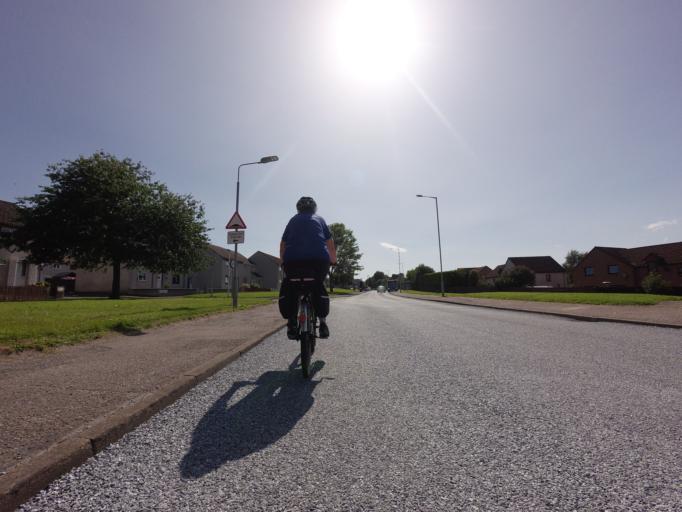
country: GB
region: Scotland
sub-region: Highland
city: Inverness
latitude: 57.4813
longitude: -4.1501
